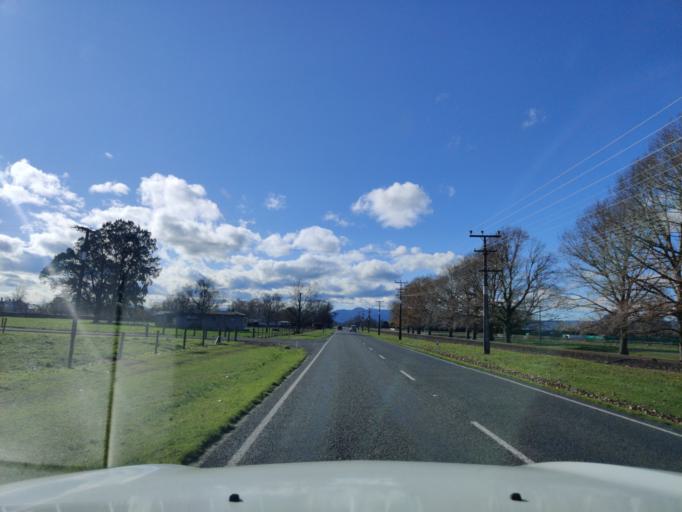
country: NZ
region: Waikato
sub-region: Matamata-Piako District
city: Matamata
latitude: -37.8430
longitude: 175.7623
